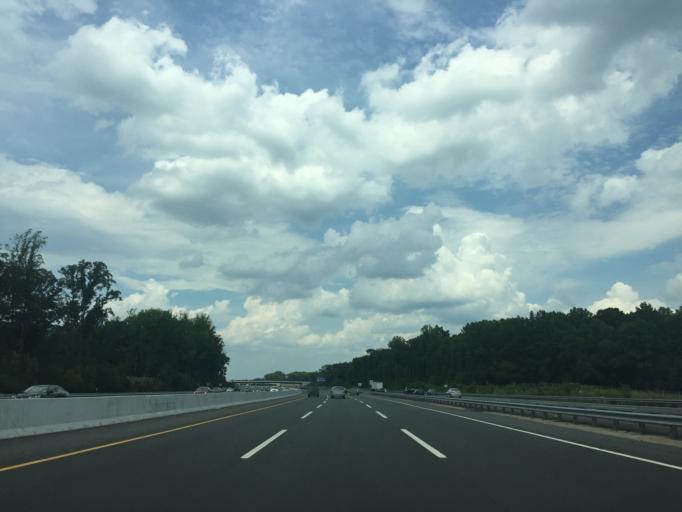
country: US
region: New Jersey
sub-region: Mercer County
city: Hightstown
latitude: 40.2487
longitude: -74.5187
